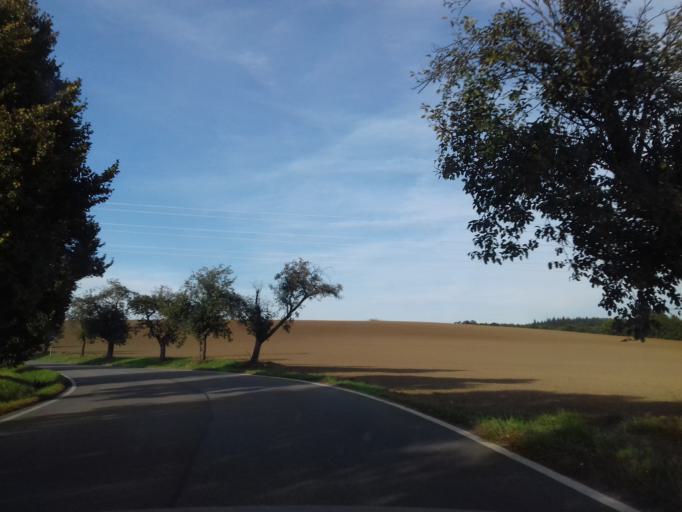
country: CZ
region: Central Bohemia
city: Kamenny Privoz
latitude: 49.8687
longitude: 14.5048
